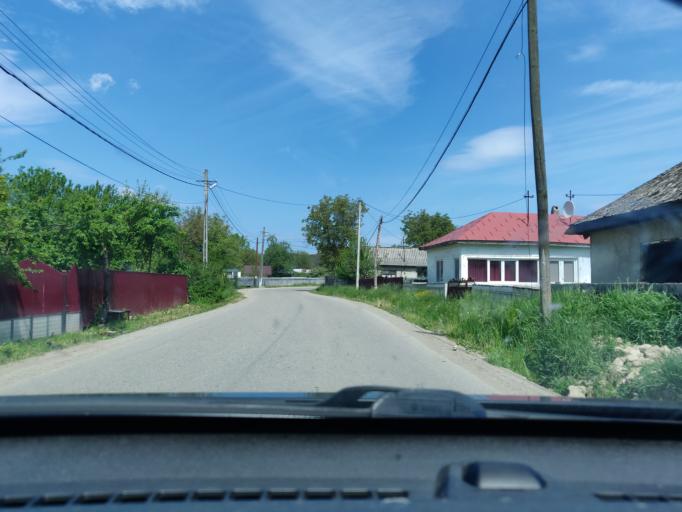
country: RO
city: Vizantea-Manastireasca
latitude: 45.9709
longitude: 26.8134
